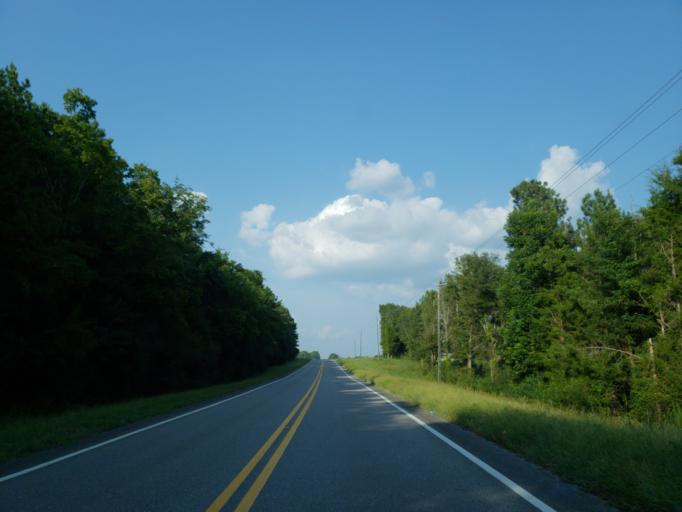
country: US
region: Alabama
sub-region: Greene County
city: Eutaw
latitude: 32.7599
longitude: -88.0112
